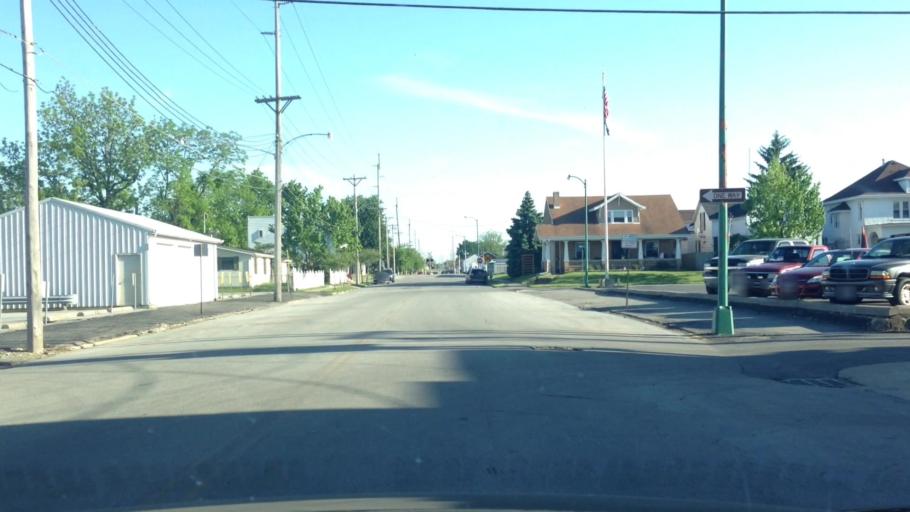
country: US
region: Ohio
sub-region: Auglaize County
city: Wapakoneta
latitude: 40.5703
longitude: -84.1928
